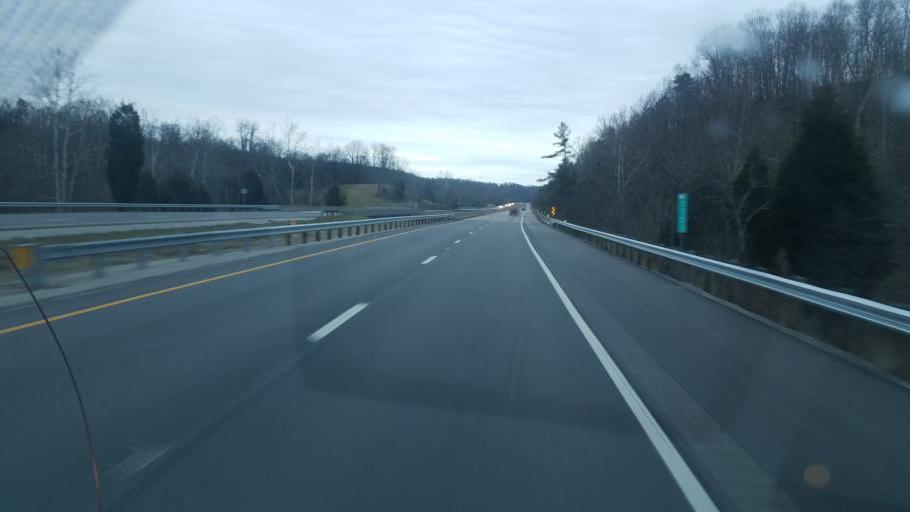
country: US
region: West Virginia
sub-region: Jackson County
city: Ripley
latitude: 38.7341
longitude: -81.6640
